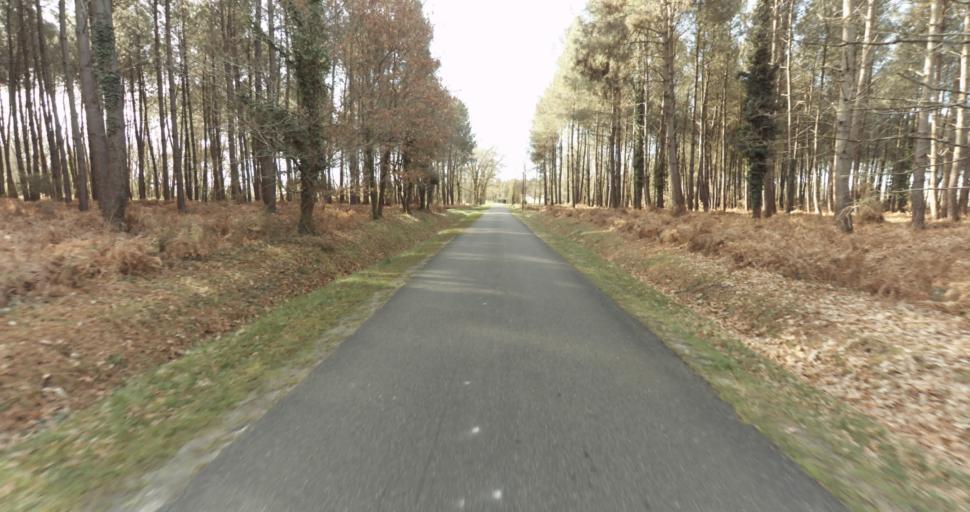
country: FR
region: Aquitaine
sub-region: Departement des Landes
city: Sarbazan
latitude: 44.0595
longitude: -0.2513
